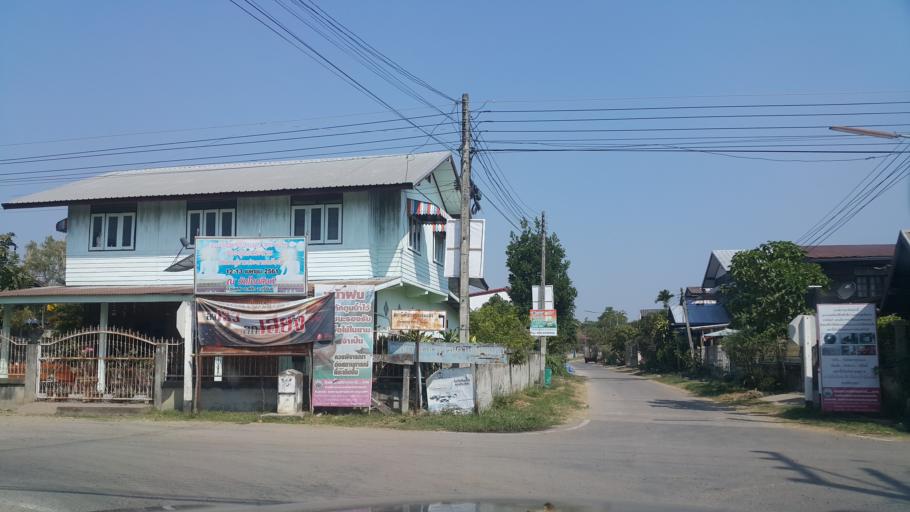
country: TH
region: Buriram
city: Satuek
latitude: 15.1312
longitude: 103.3761
